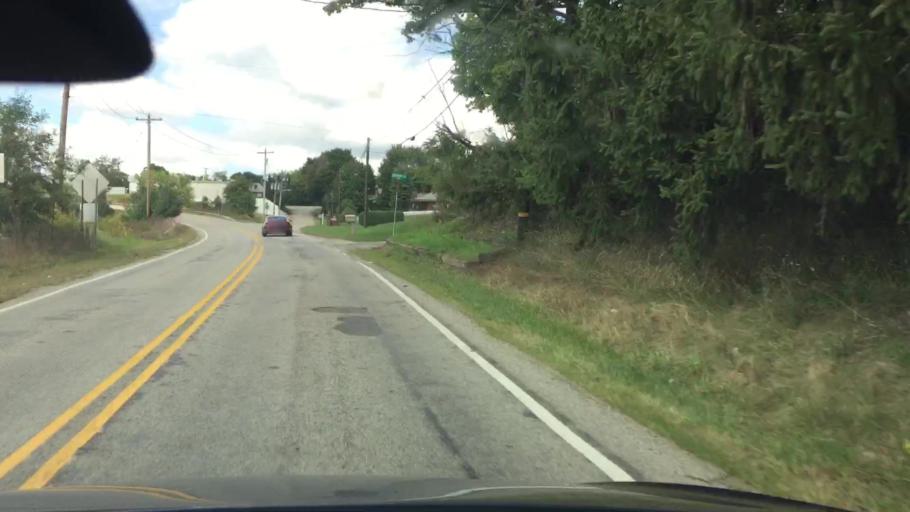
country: US
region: Pennsylvania
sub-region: Butler County
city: Meadowood
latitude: 40.8410
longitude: -79.8799
